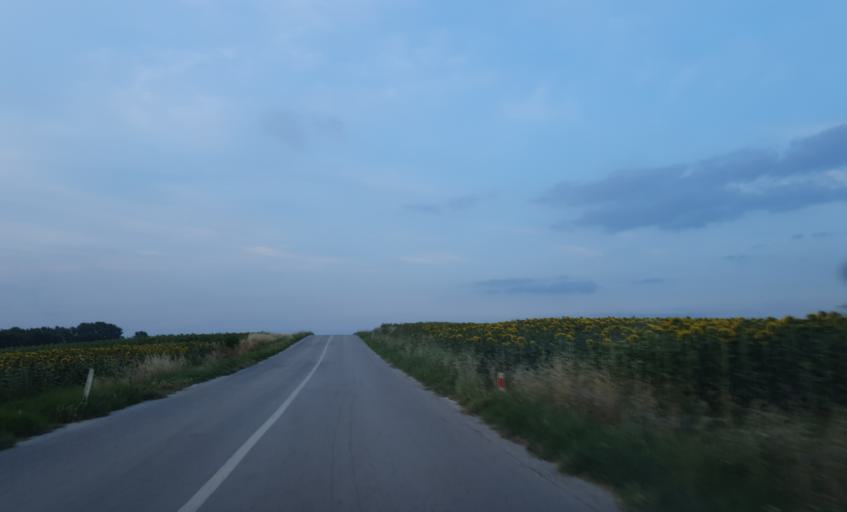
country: TR
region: Tekirdag
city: Beyazkoy
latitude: 41.3961
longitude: 27.6336
